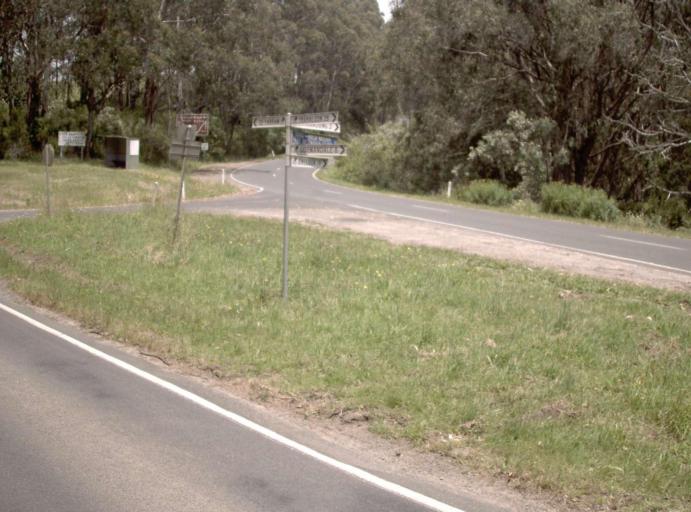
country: AU
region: Victoria
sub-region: Latrobe
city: Traralgon
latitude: -38.3498
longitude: 146.7146
